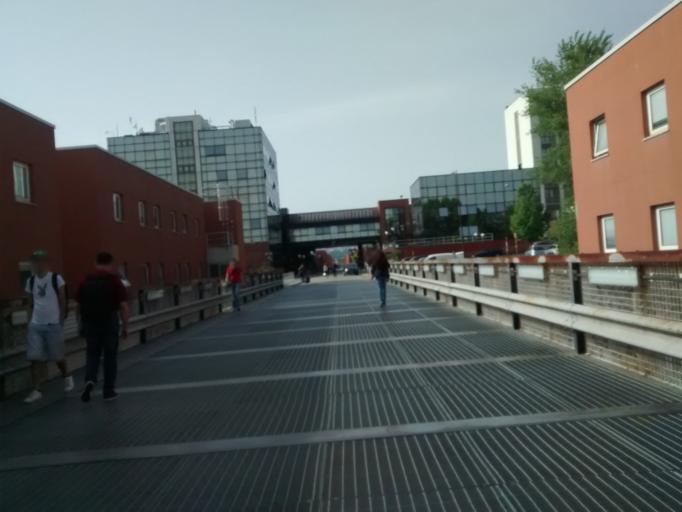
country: IT
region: Calabria
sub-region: Provincia di Cosenza
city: Arcavacata
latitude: 39.3628
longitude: 16.2260
